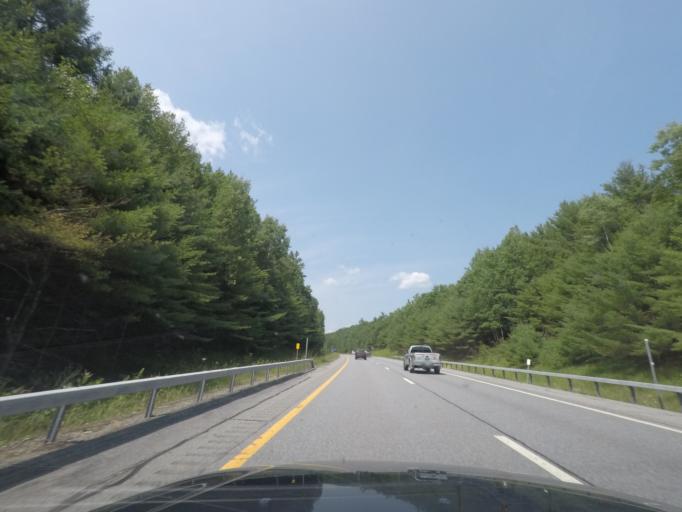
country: US
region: New York
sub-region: Warren County
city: Warrensburg
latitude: 43.5204
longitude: -73.7385
